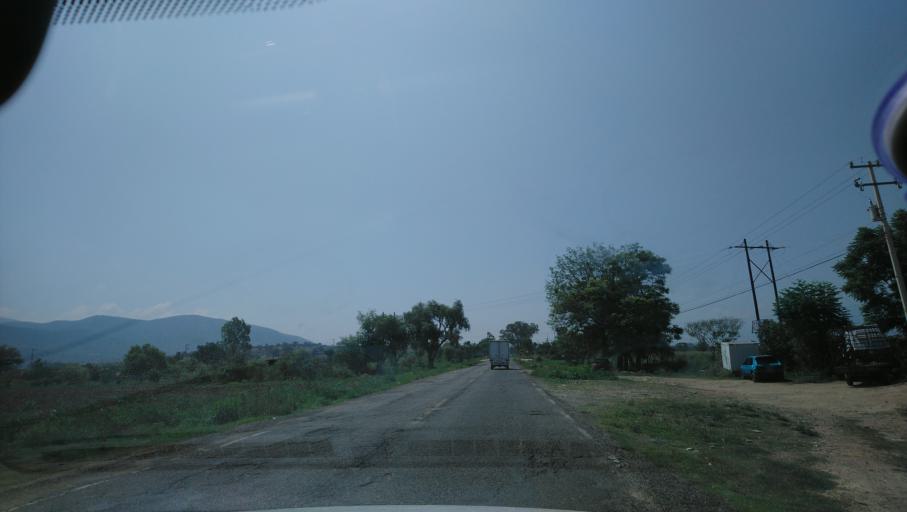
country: MX
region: Oaxaca
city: Santa Maria del Tule
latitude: 17.0416
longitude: -96.6255
